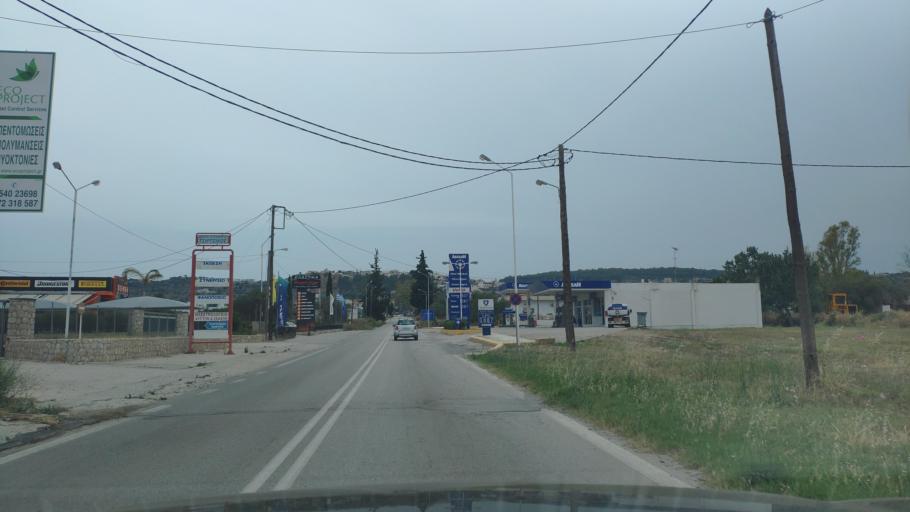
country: GR
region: Peloponnese
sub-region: Nomos Argolidos
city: Kranidi
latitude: 37.3937
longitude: 23.1571
